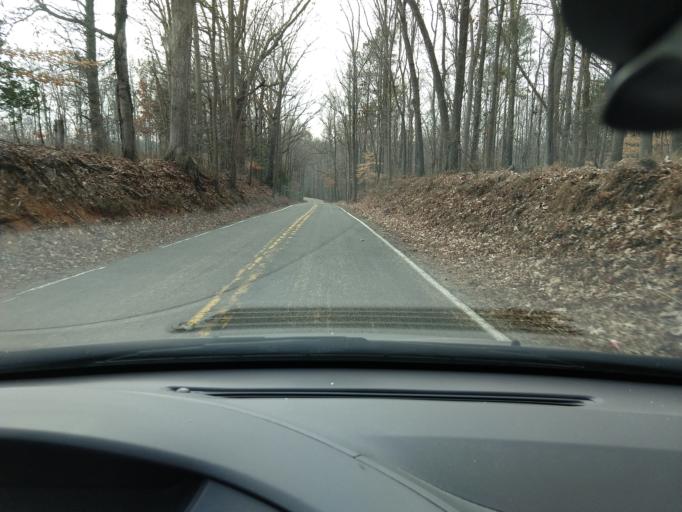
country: US
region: Virginia
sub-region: Henrico County
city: Fort Lee
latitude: 37.4226
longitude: -77.2434
